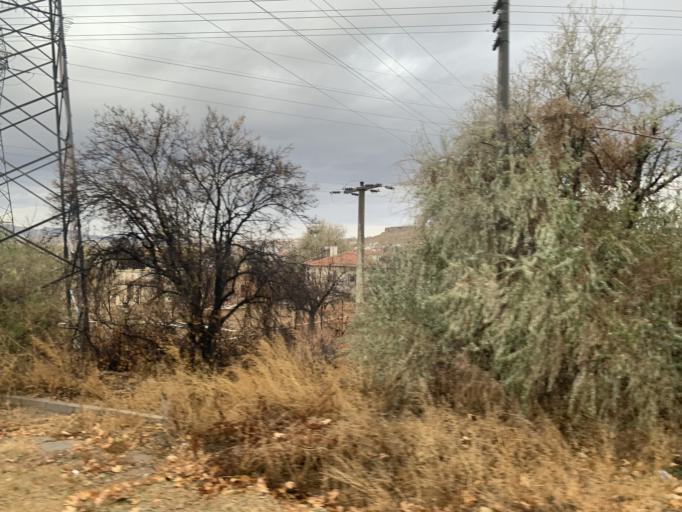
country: TR
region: Nevsehir
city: Avanos
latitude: 38.7183
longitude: 34.8604
